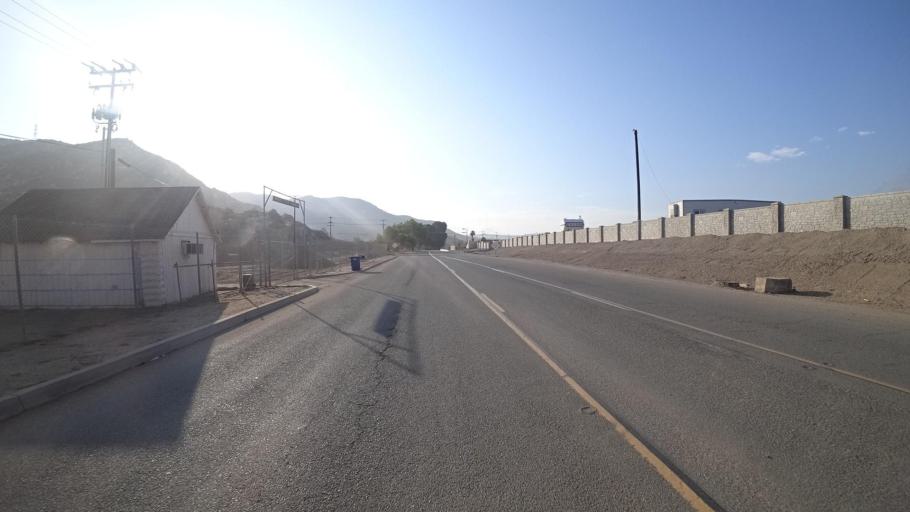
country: US
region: California
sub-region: San Diego County
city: Eucalyptus Hills
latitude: 32.9024
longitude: -116.9325
